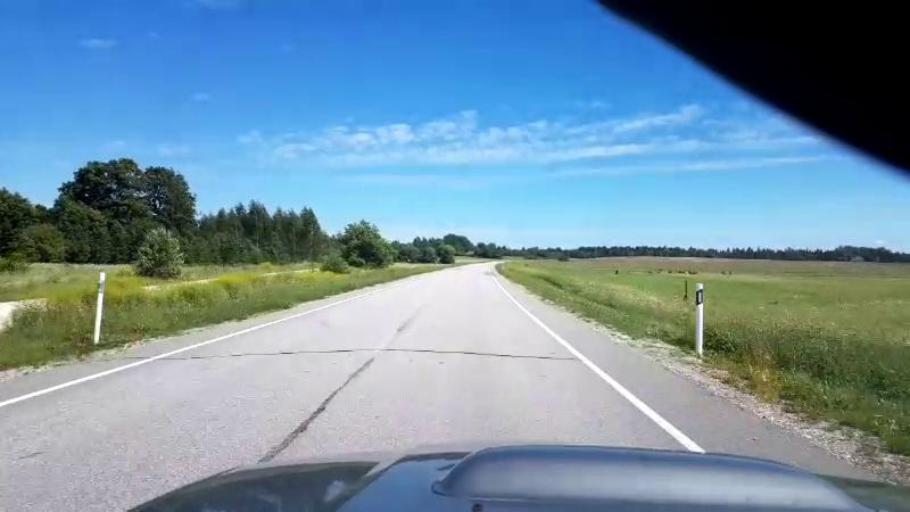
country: EE
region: Jaervamaa
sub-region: Koeru vald
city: Koeru
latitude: 58.9785
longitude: 26.0891
